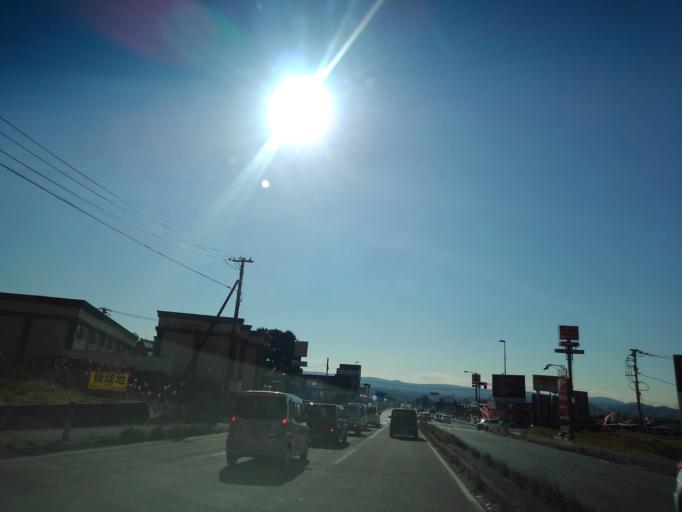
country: JP
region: Chiba
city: Kimitsu
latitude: 35.3342
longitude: 139.9226
